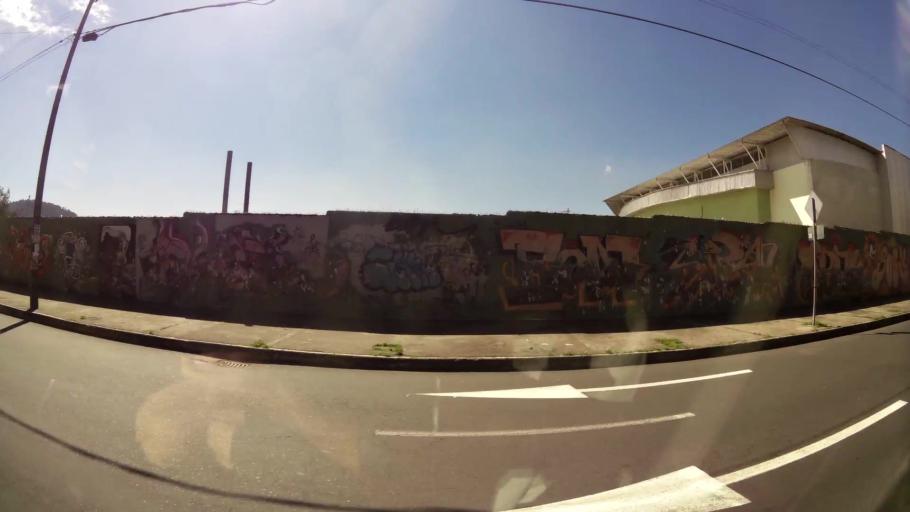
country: EC
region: Pichincha
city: Quito
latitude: -0.2451
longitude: -78.5307
